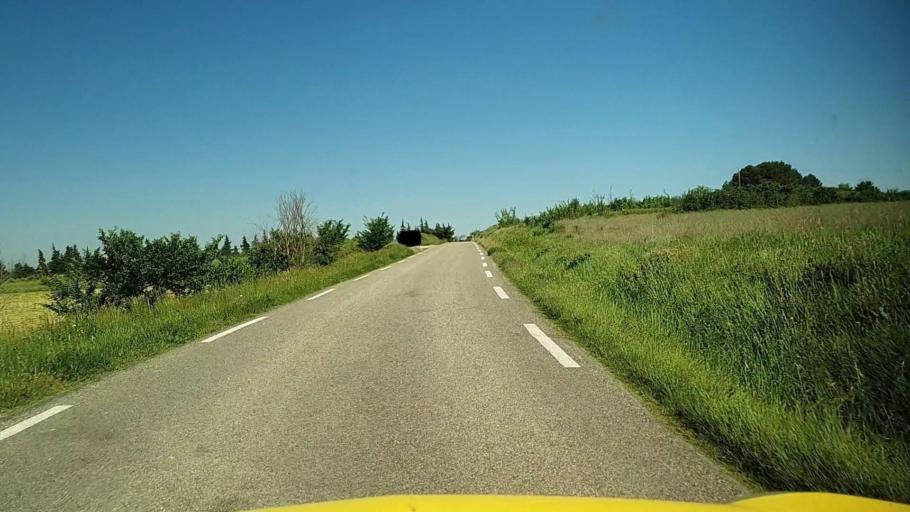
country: FR
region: Languedoc-Roussillon
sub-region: Departement du Gard
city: Saint-Chaptes
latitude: 43.9500
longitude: 4.3059
